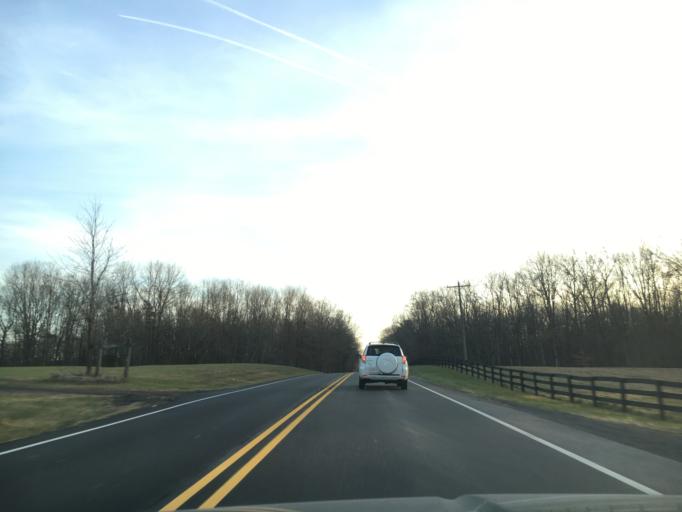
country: US
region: Virginia
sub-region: Orange County
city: Orange
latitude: 38.2822
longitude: -77.9566
